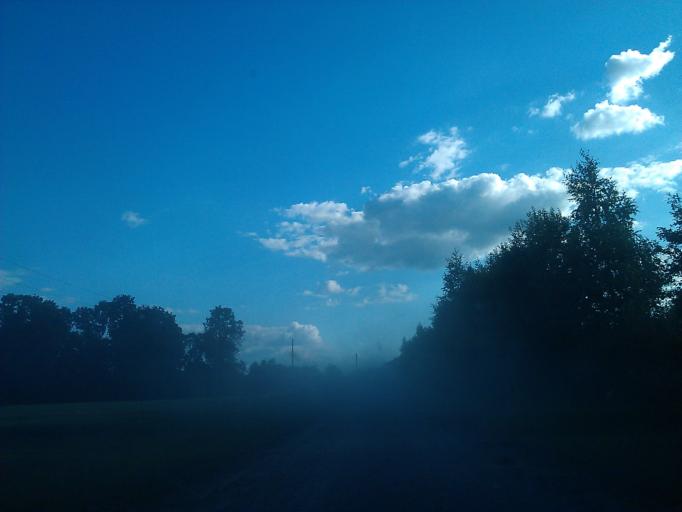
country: LV
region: Varaklani
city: Varaklani
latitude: 56.5682
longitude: 26.7834
